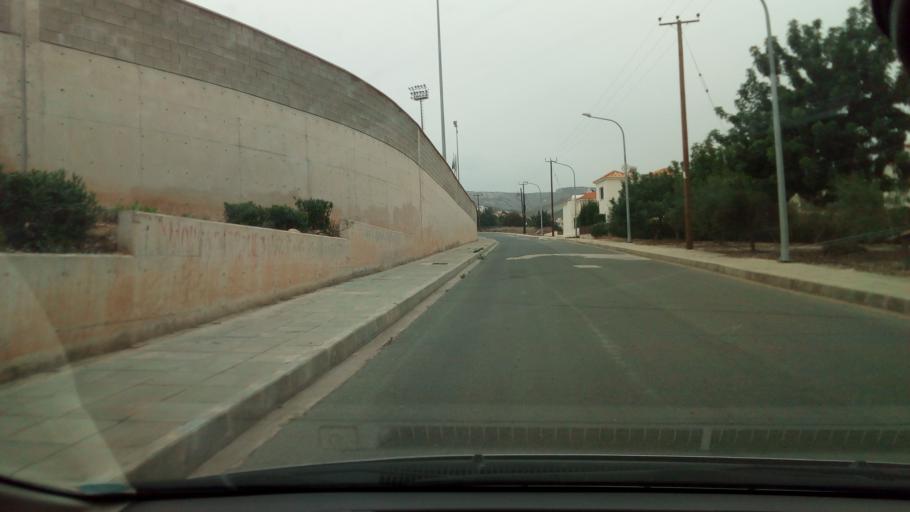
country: CY
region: Pafos
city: Pegeia
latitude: 34.8740
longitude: 32.3824
